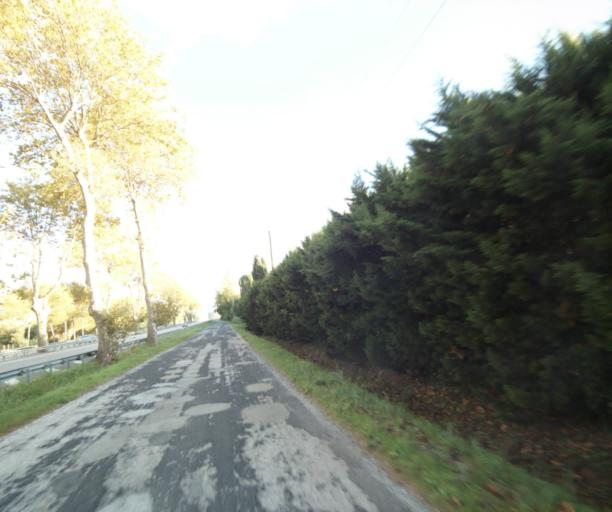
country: FR
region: Languedoc-Roussillon
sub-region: Departement des Pyrenees-Orientales
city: Elne
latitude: 42.5797
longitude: 2.9903
